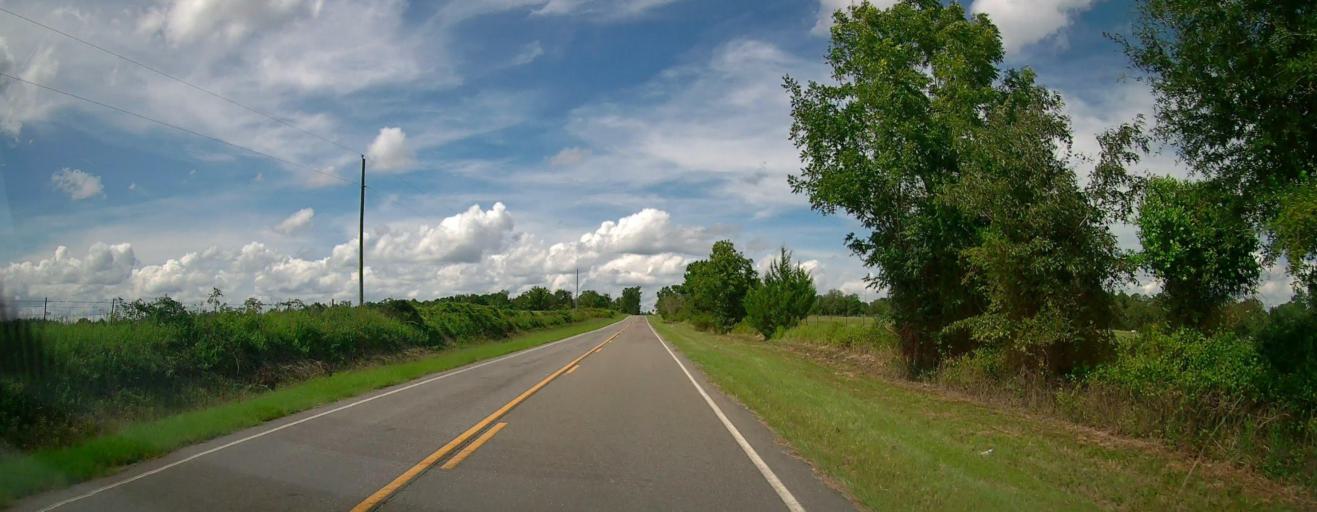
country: US
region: Georgia
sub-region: Taylor County
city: Butler
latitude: 32.4705
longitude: -84.2011
